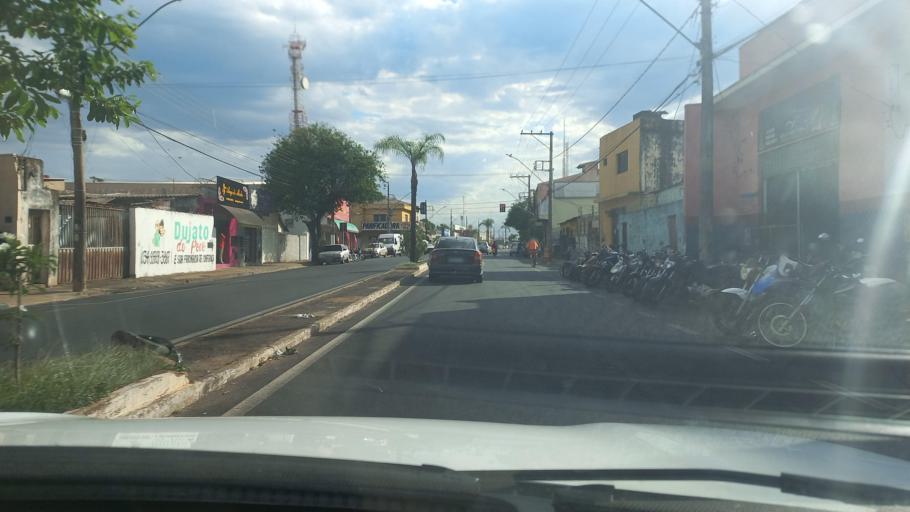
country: BR
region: Minas Gerais
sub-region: Uberaba
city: Uberaba
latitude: -19.7653
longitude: -47.9191
